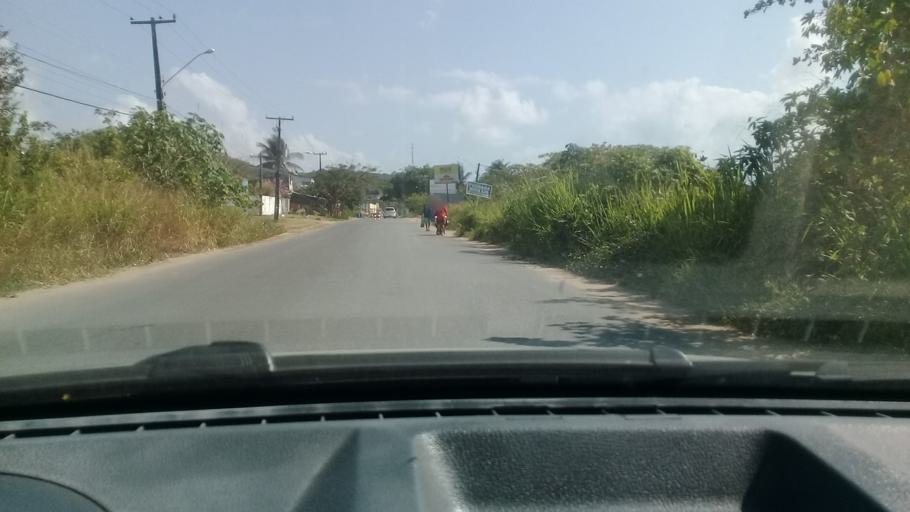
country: BR
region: Pernambuco
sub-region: Itamaraca
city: Itamaraca
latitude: -7.7910
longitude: -34.8412
